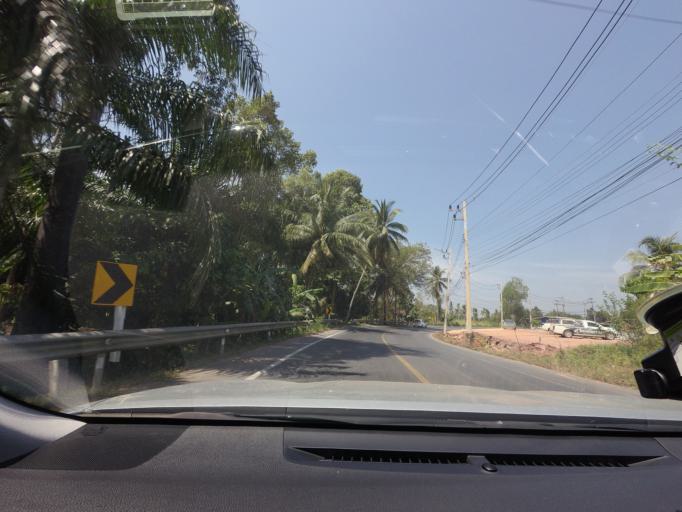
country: TH
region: Surat Thani
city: Phunphin
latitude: 9.1899
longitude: 99.2599
